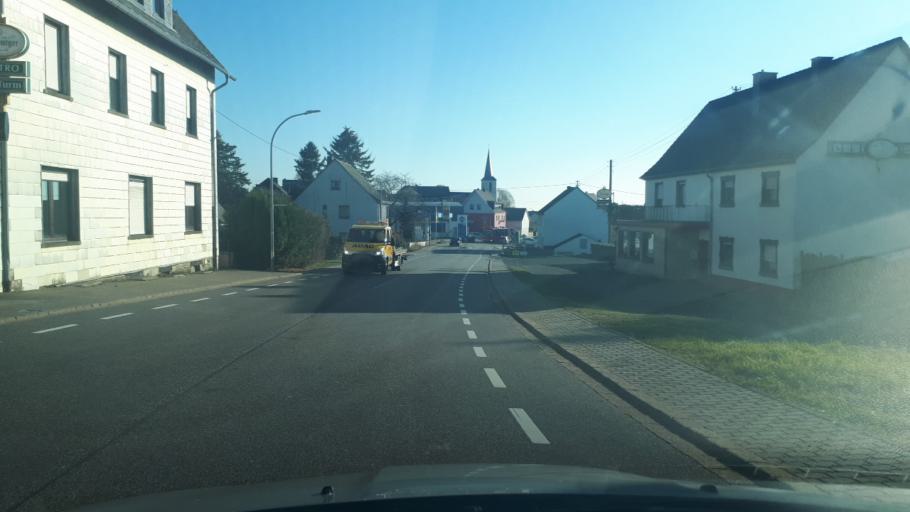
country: DE
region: Rheinland-Pfalz
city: Buchel
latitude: 50.1751
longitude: 7.0813
